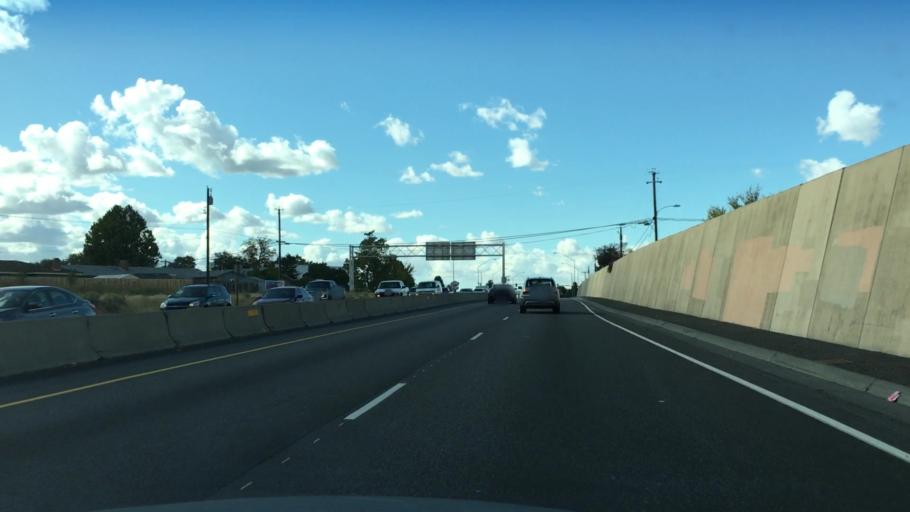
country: US
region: Washington
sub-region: Benton County
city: Kennewick
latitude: 46.2153
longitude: -119.1464
